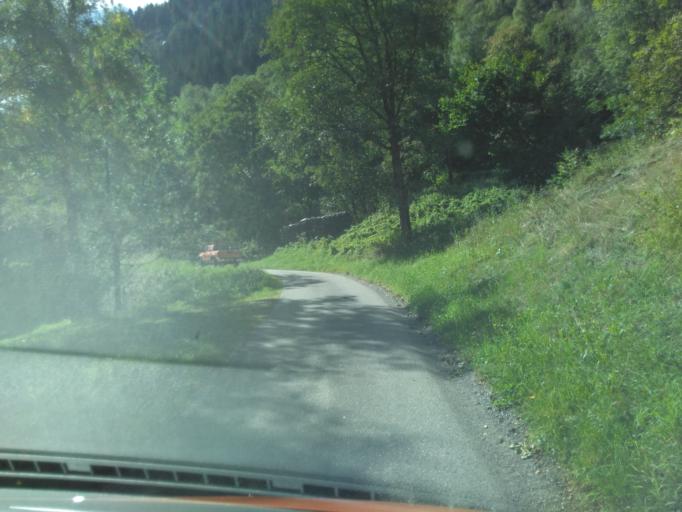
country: CH
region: Grisons
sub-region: Moesa District
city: Cauco
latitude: 46.3699
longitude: 9.1254
